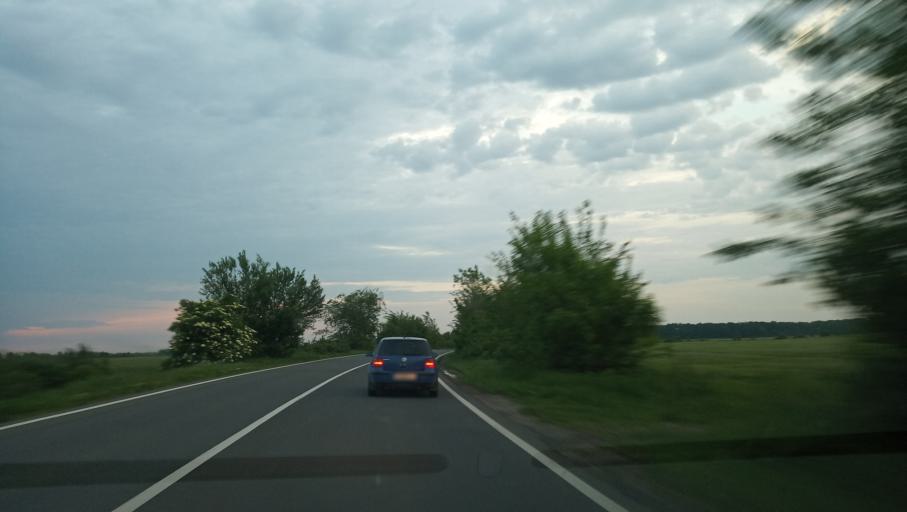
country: RO
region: Timis
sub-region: Comuna Padureni
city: Padureni
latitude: 45.6125
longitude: 21.1952
